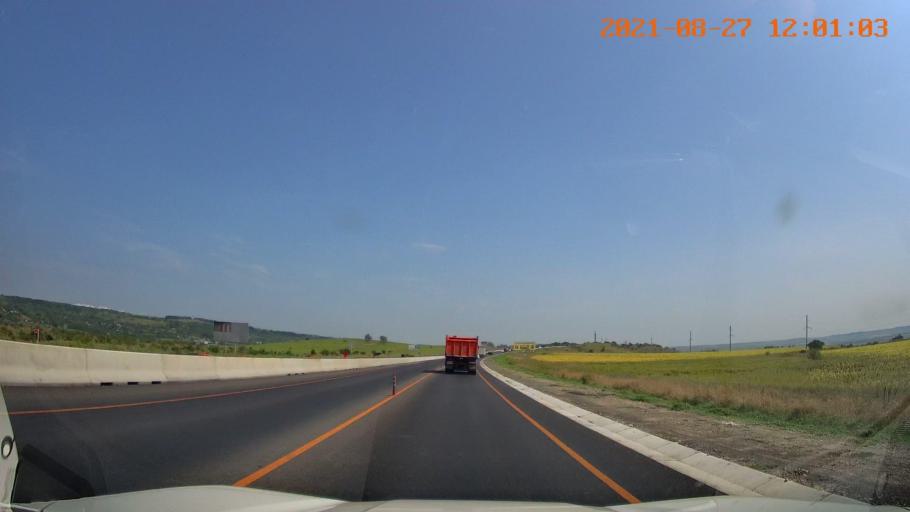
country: RU
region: Stavropol'skiy
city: Tatarka
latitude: 44.9495
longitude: 41.9325
